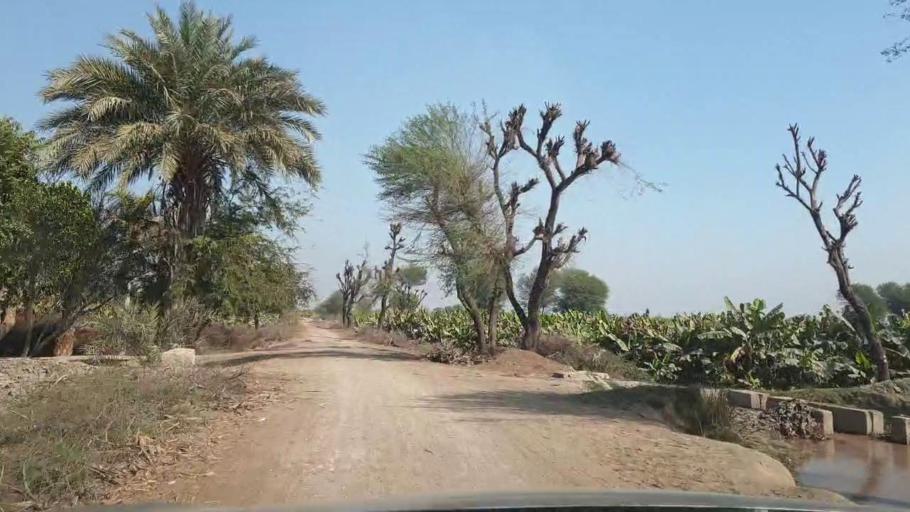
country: PK
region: Sindh
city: Tando Allahyar
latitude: 25.5916
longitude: 68.6513
